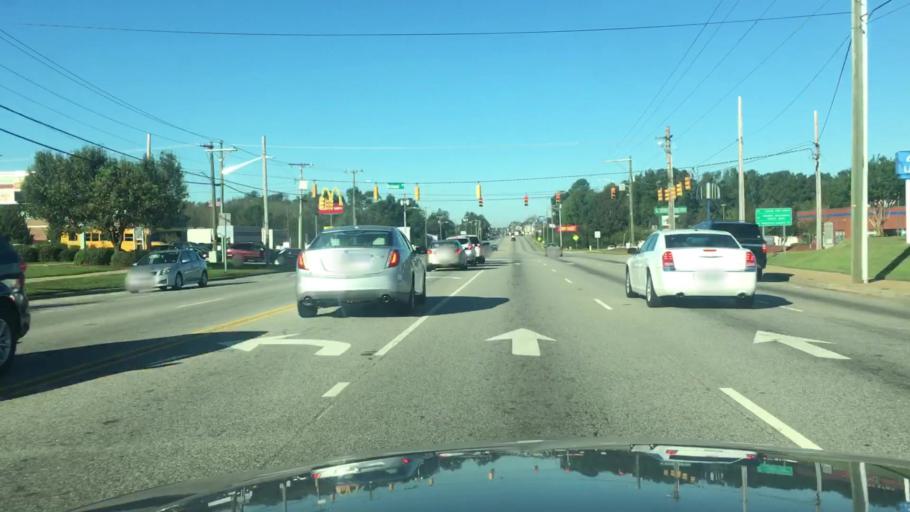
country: US
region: North Carolina
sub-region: Cumberland County
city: Fayetteville
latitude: 35.0438
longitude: -78.9467
